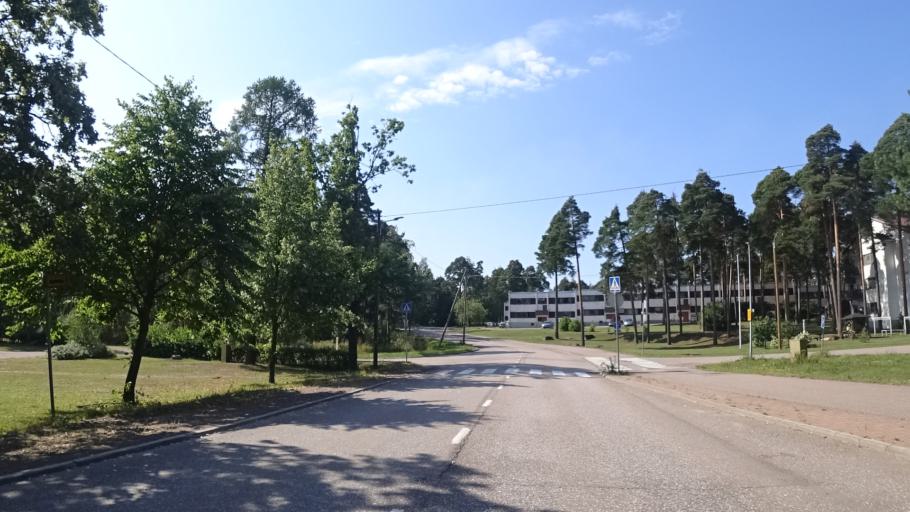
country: FI
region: Kymenlaakso
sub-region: Kotka-Hamina
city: Karhula
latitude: 60.4963
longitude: 26.9597
